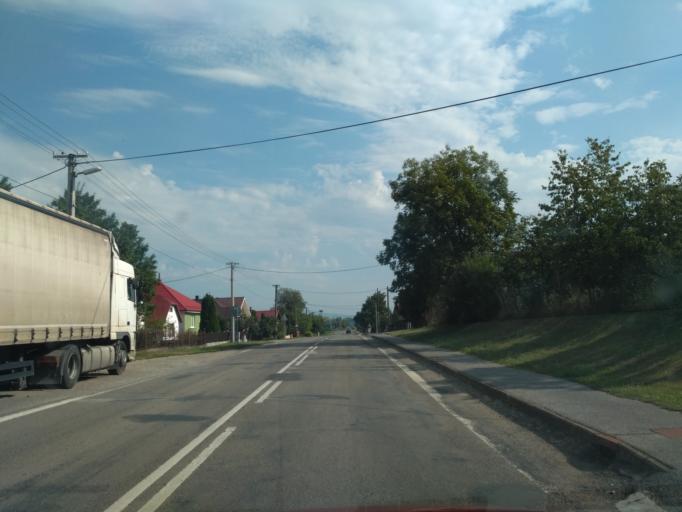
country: SK
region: Kosicky
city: Kosice
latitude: 48.8267
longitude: 21.2975
